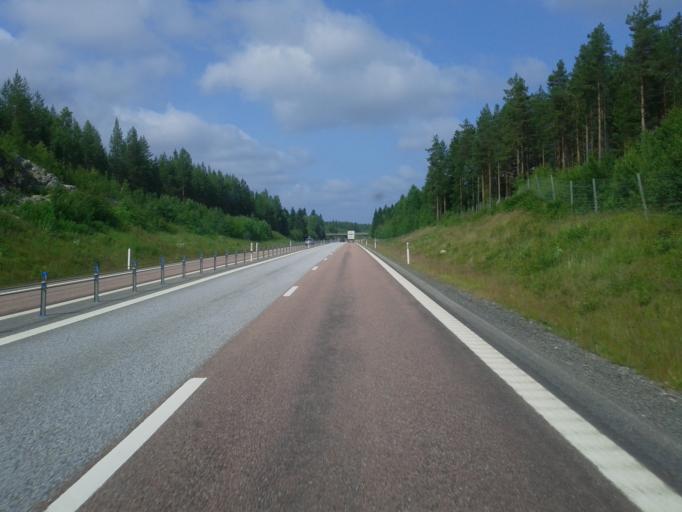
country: SE
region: Vaesterbotten
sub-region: Skelleftea Kommun
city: Soedra Bergsbyn
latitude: 64.6941
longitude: 21.0247
